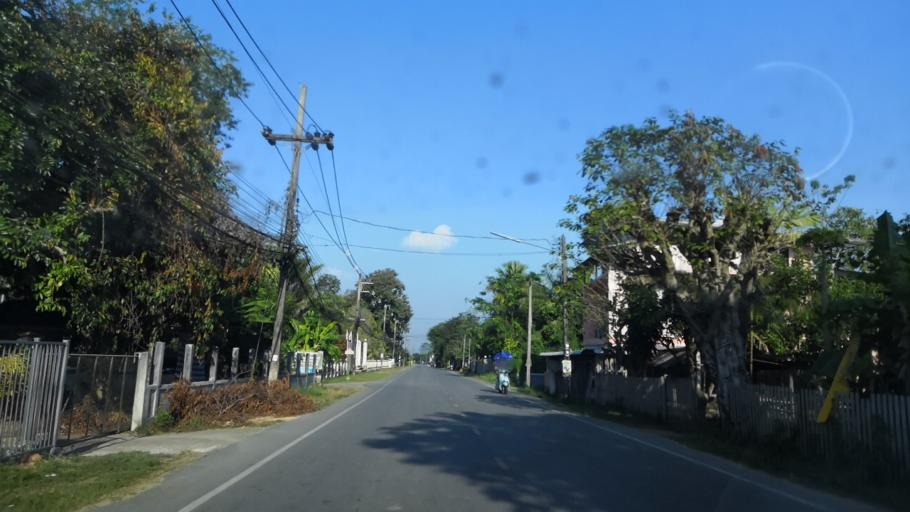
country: TH
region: Chiang Rai
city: Wiang Chai
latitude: 19.9388
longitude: 99.9106
